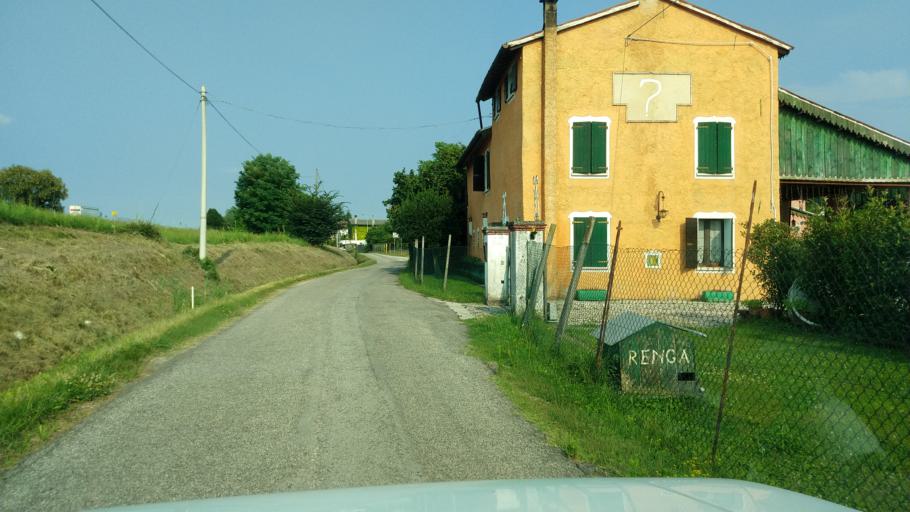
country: IT
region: Veneto
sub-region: Provincia di Vicenza
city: Nove
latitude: 45.7379
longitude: 11.6871
